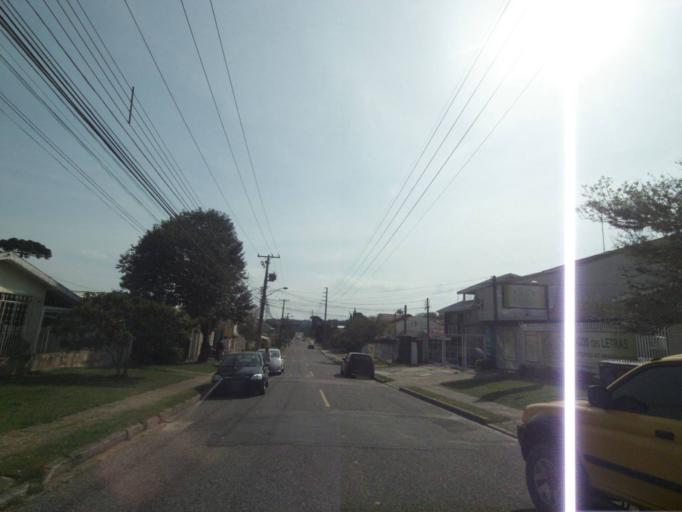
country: BR
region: Parana
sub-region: Curitiba
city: Curitiba
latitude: -25.4595
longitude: -49.3081
